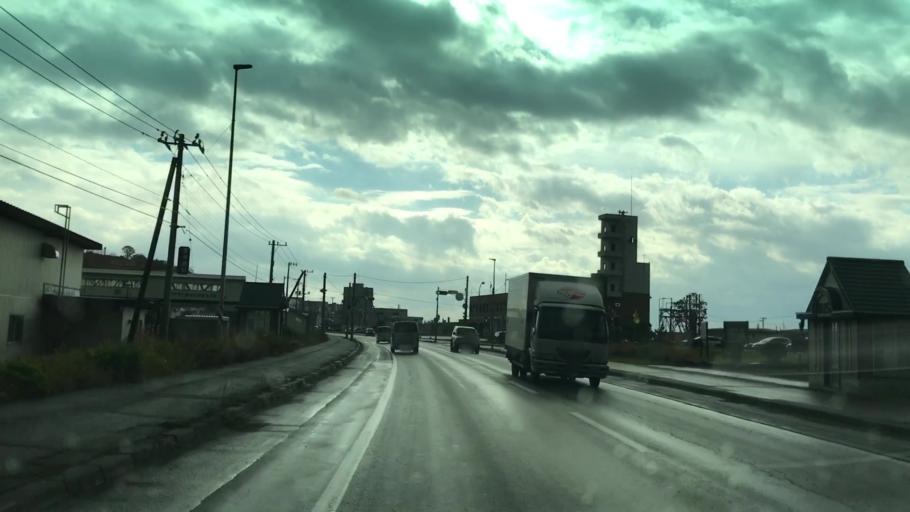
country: JP
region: Hokkaido
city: Shizunai-furukawacho
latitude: 42.1691
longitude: 142.7688
